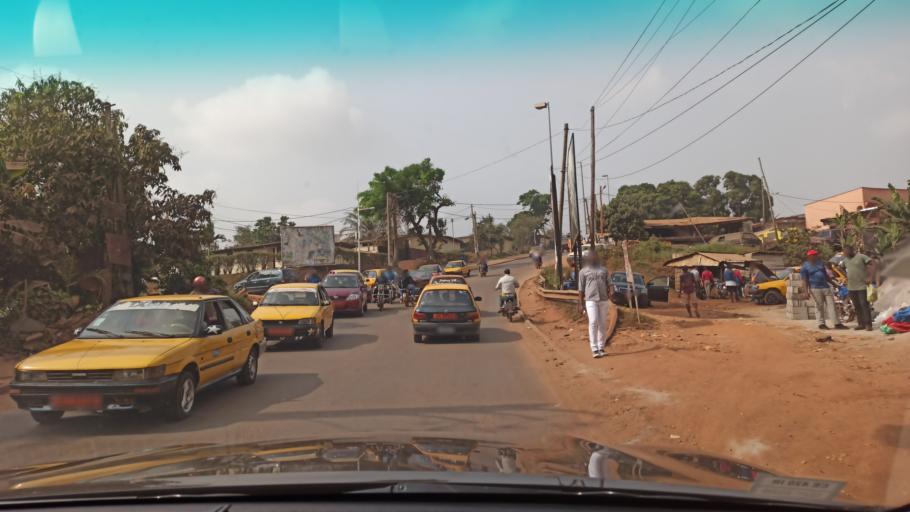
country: CM
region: Centre
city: Yaounde
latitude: 3.8792
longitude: 11.4916
